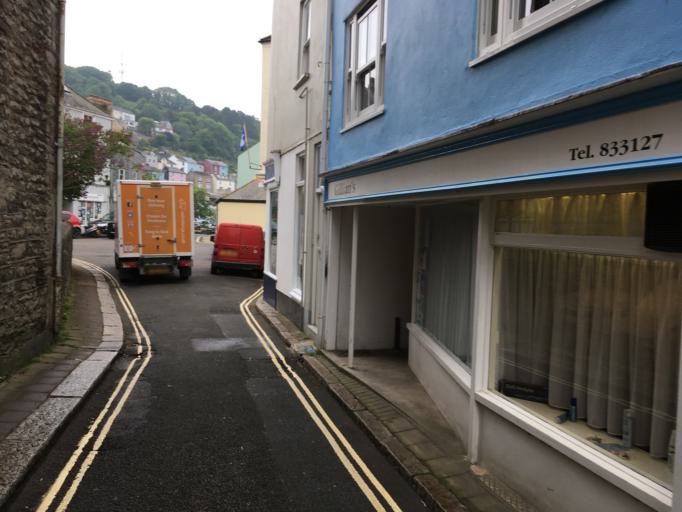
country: GB
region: England
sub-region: Devon
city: Dartmouth
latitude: 50.3527
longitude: -3.5799
